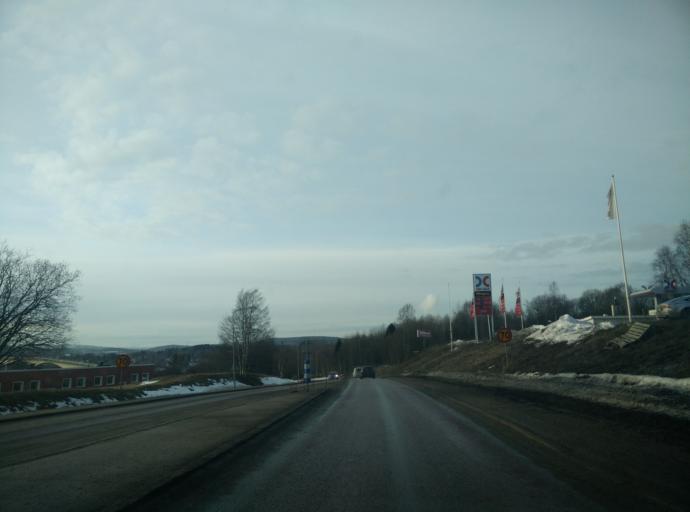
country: SE
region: Vaesternorrland
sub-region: Sundsvalls Kommun
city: Johannedal
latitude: 62.4320
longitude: 17.4148
